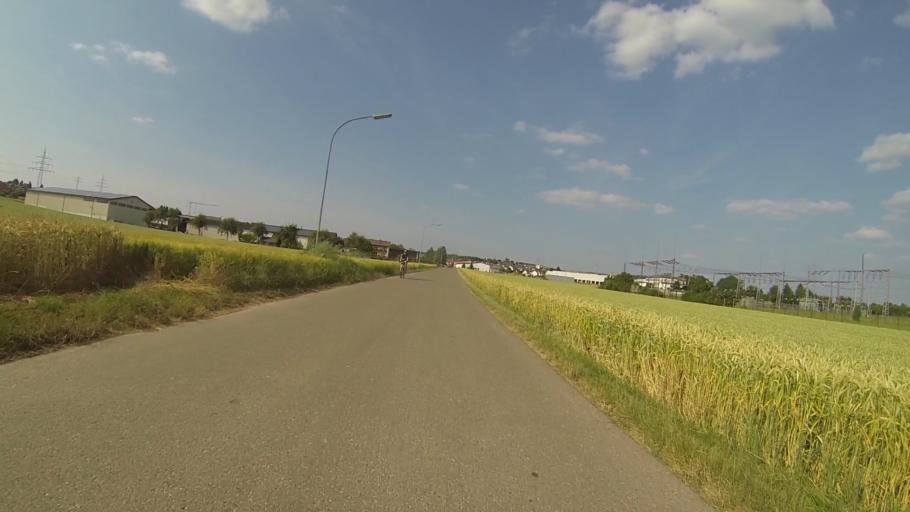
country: DE
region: Baden-Wuerttemberg
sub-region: Regierungsbezirk Stuttgart
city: Niederstotzingen
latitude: 48.5307
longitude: 10.2306
